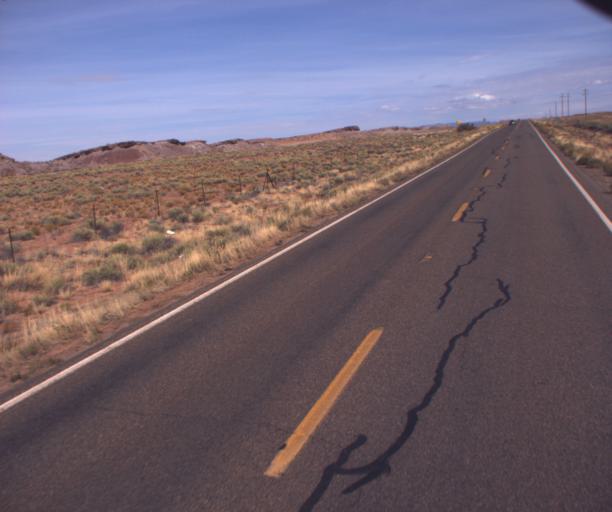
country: US
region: Arizona
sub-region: Apache County
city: Many Farms
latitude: 36.4990
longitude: -109.4855
